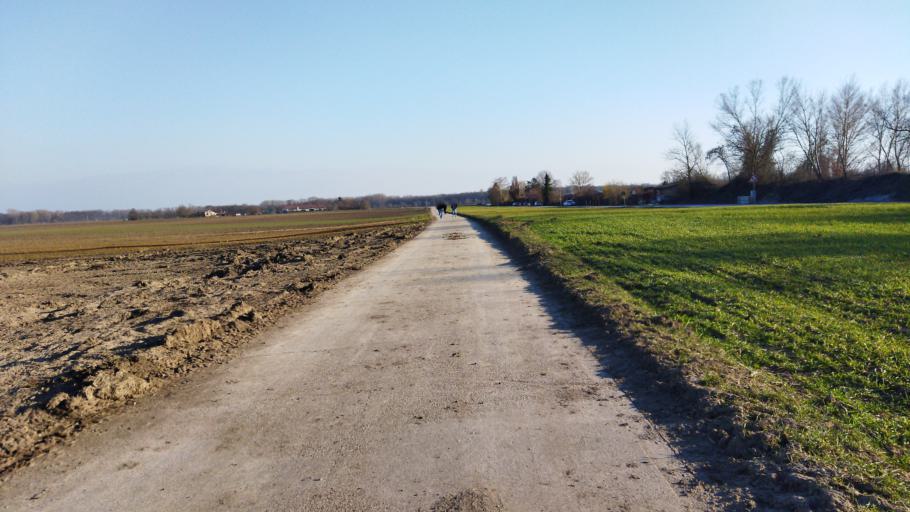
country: DE
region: Rheinland-Pfalz
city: Waldsee
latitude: 49.4091
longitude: 8.4478
